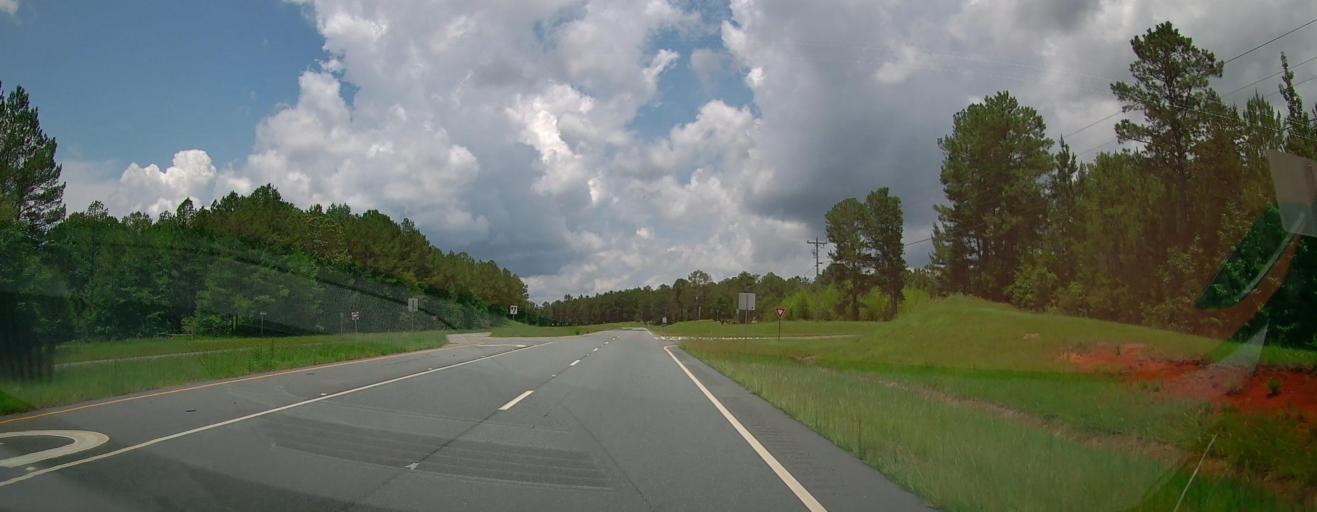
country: US
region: Georgia
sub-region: Upson County
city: Thomaston
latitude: 32.8031
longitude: -84.2757
